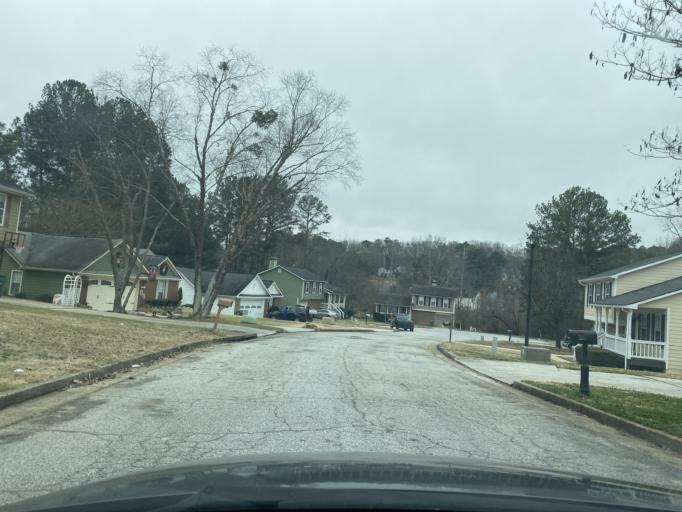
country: US
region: Georgia
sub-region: DeKalb County
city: Pine Mountain
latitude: 33.6892
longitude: -84.1616
